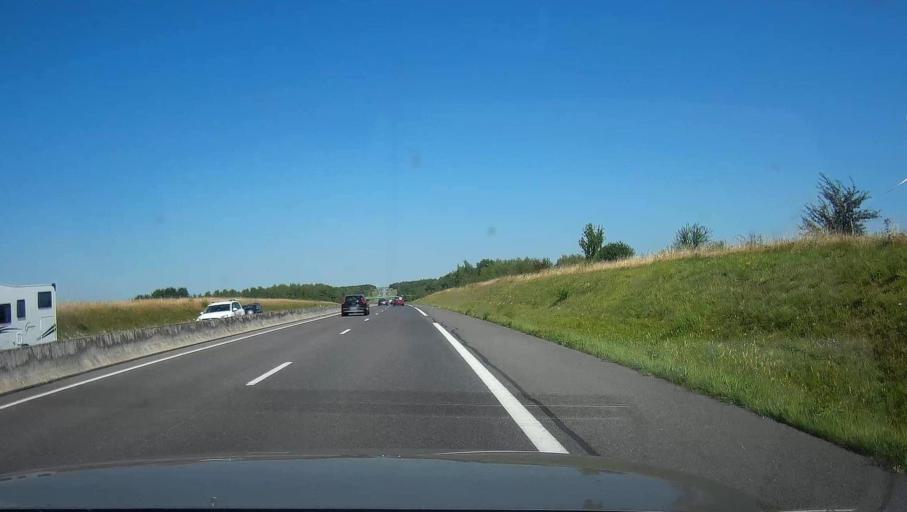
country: FR
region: Champagne-Ardenne
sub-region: Departement de l'Aube
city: Arcis-sur-Aube
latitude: 48.4774
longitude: 4.1655
